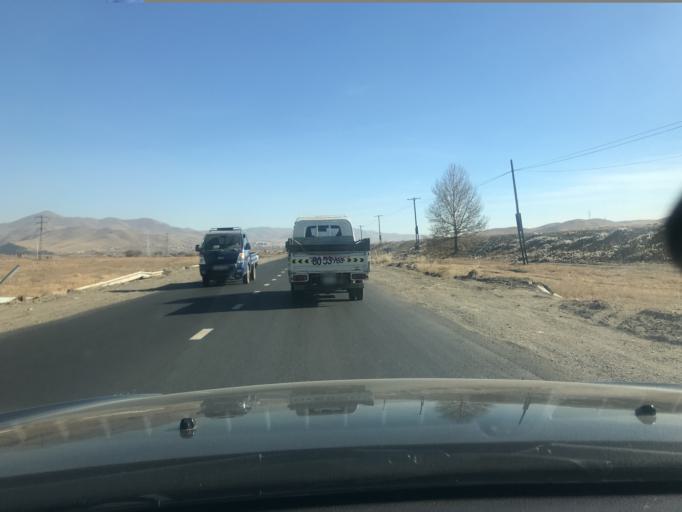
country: MN
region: Ulaanbaatar
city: Ulaanbaatar
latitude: 47.8970
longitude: 107.0469
